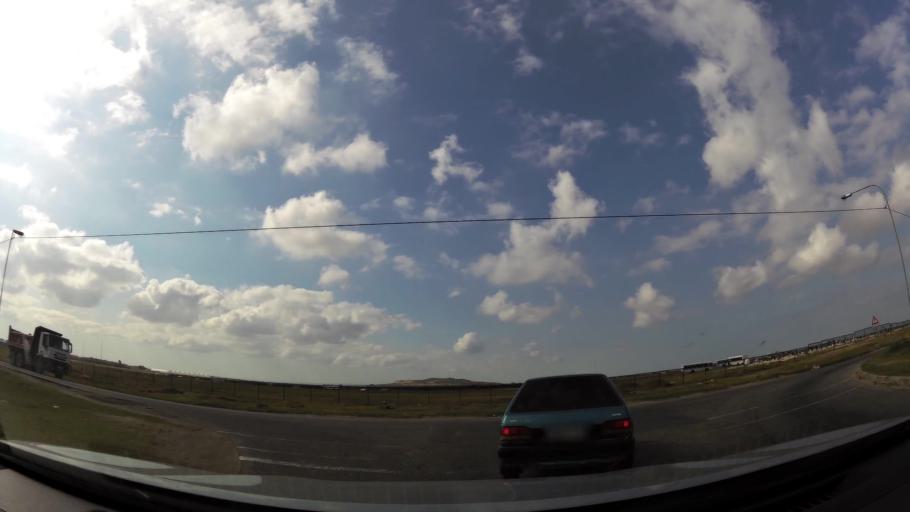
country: ZA
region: Eastern Cape
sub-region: Nelson Mandela Bay Metropolitan Municipality
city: Port Elizabeth
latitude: -33.7851
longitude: 25.5928
